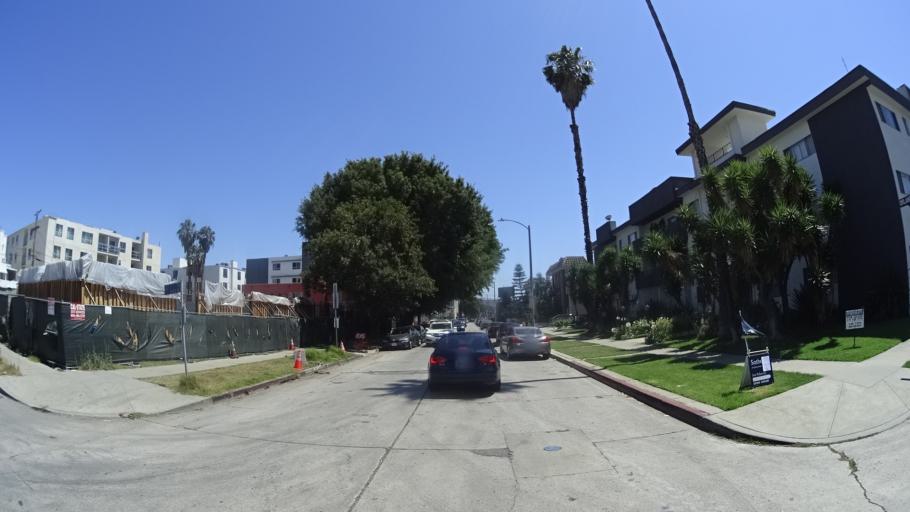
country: US
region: California
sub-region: Los Angeles County
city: West Hollywood
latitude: 34.0745
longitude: -118.3732
